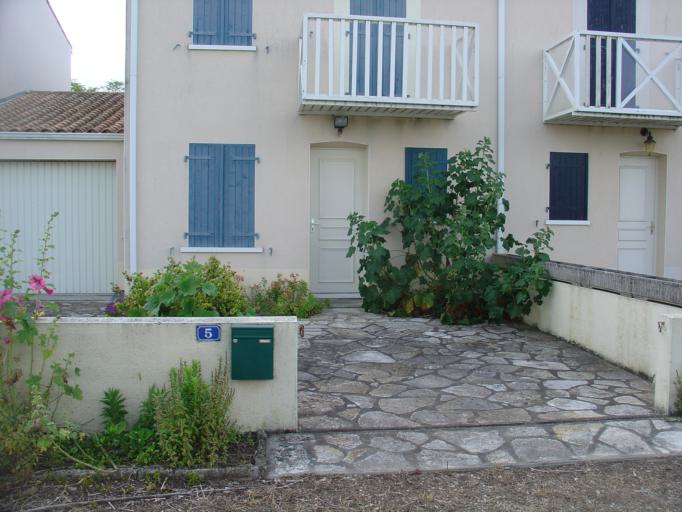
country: FR
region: Poitou-Charentes
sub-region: Departement de la Charente-Maritime
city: Boyard-Ville
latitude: 45.9640
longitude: -1.2433
